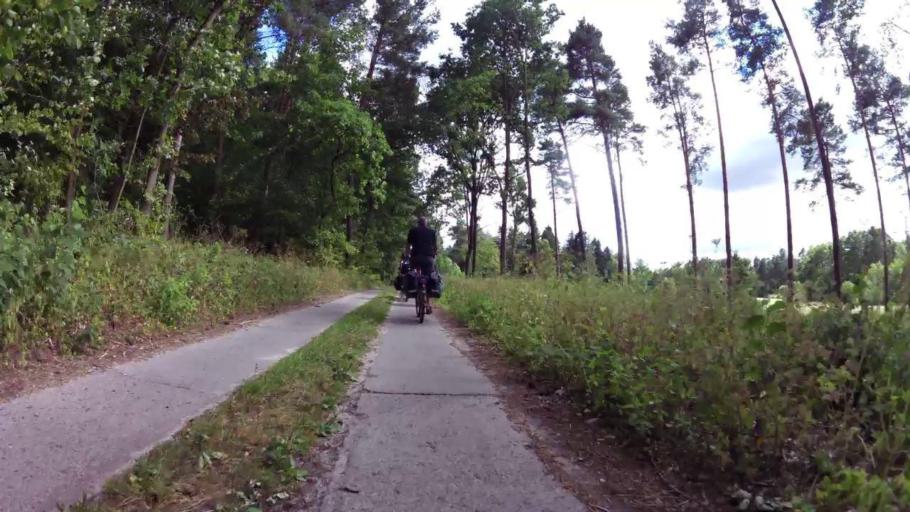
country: PL
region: West Pomeranian Voivodeship
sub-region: Powiat lobeski
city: Lobez
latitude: 53.6423
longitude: 15.5822
